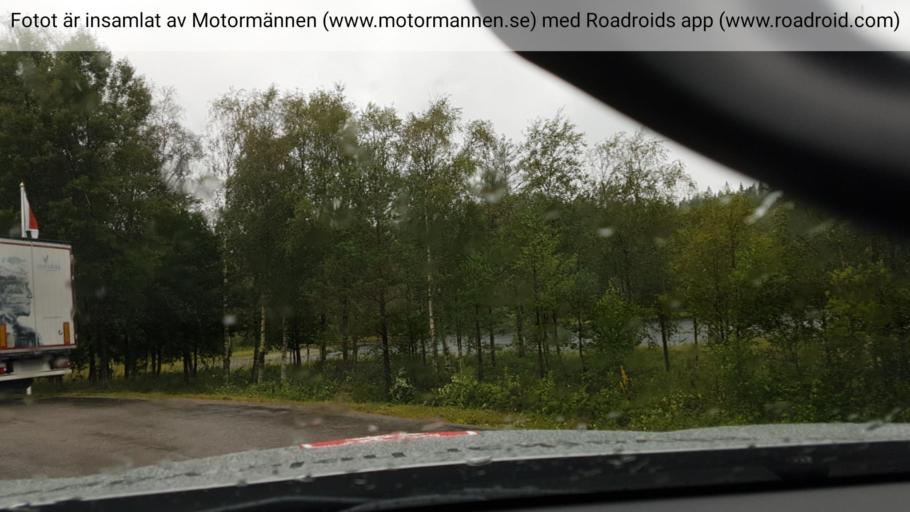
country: SE
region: Vaestra Goetaland
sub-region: Dals-Ed Kommun
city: Ed
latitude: 58.8784
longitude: 11.8289
